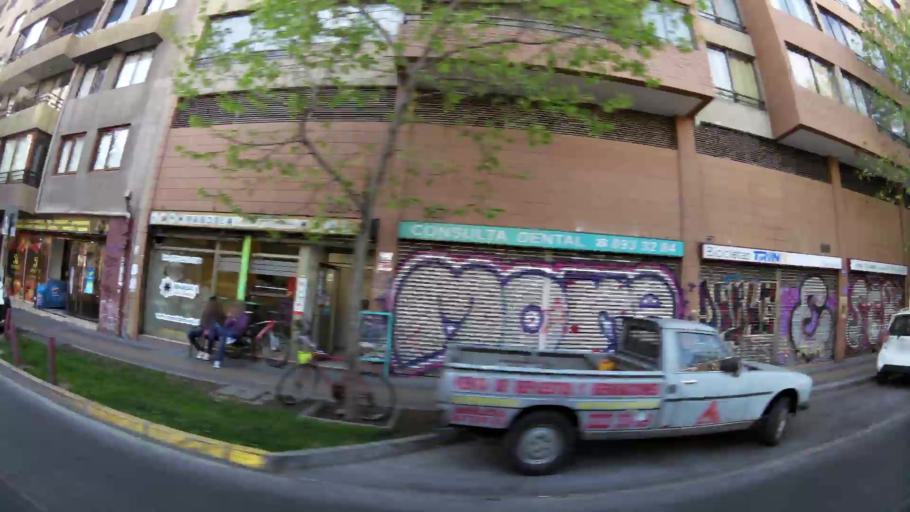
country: CL
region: Santiago Metropolitan
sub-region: Provincia de Santiago
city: Santiago
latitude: -33.4488
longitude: -70.6374
